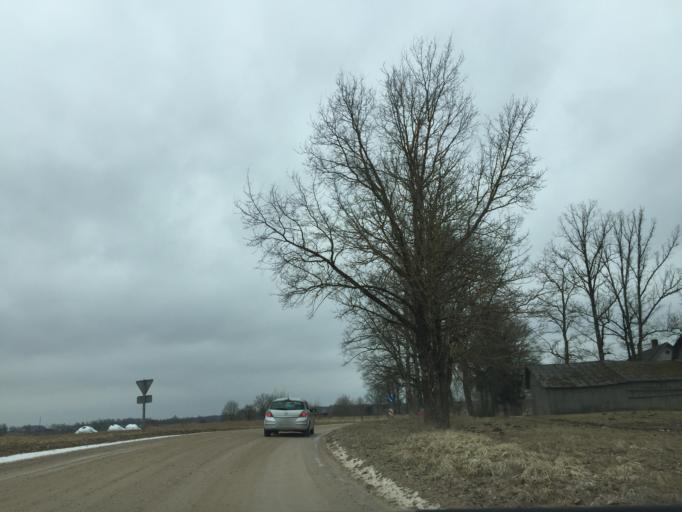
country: LV
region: Kegums
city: Kegums
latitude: 56.7694
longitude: 24.7721
